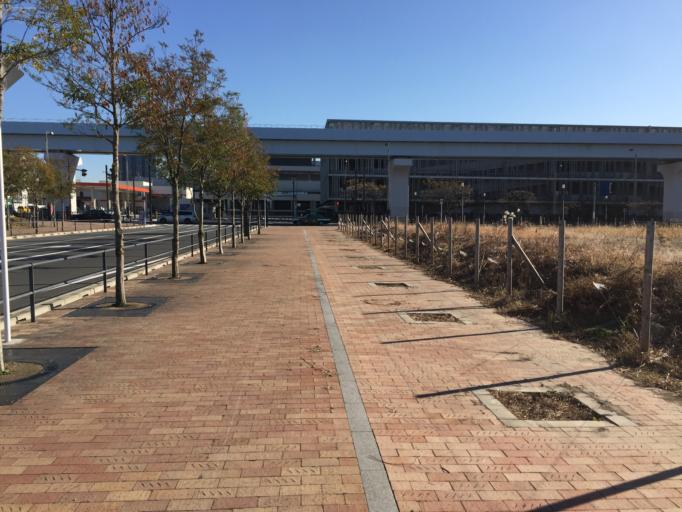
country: JP
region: Tokyo
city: Tokyo
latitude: 35.6475
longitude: 139.7869
